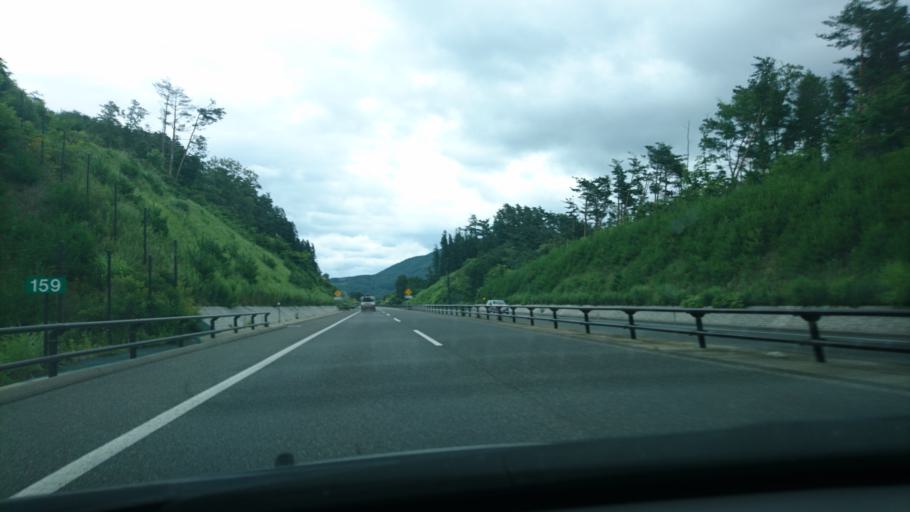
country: JP
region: Iwate
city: Ofunato
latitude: 39.0279
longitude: 141.6594
